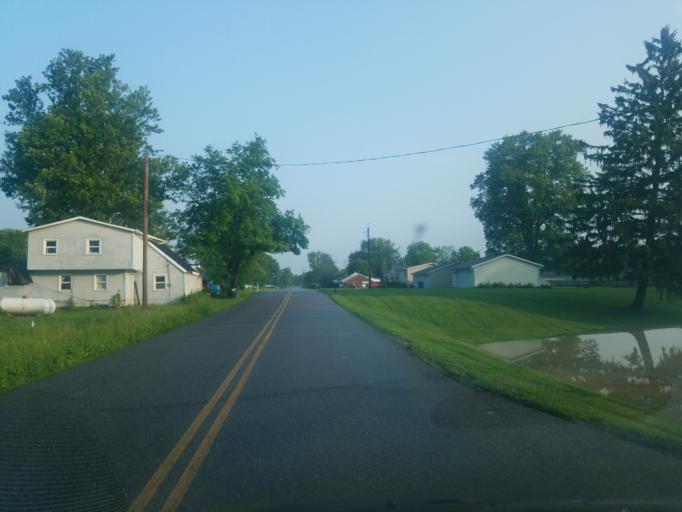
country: US
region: Ohio
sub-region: Stark County
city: Minerva
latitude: 40.7029
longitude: -81.0787
